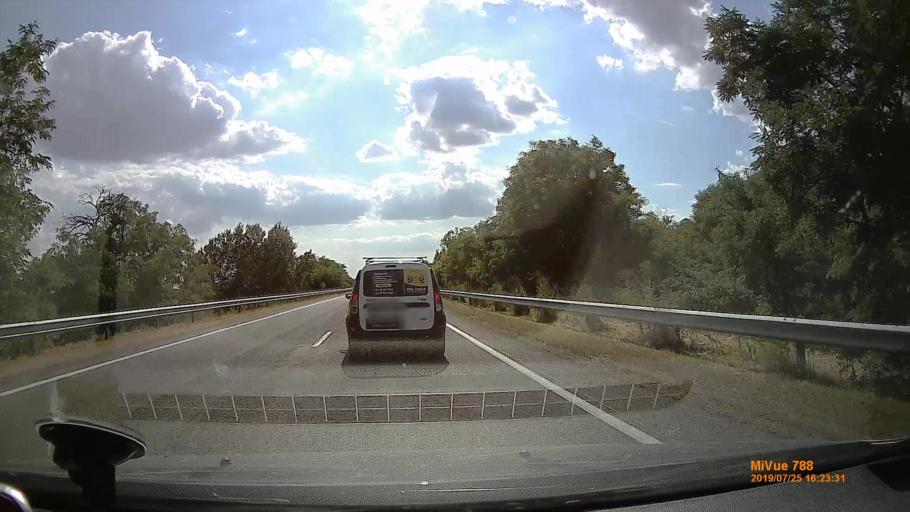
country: HU
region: Heves
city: Kompolt
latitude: 47.7542
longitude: 20.1768
